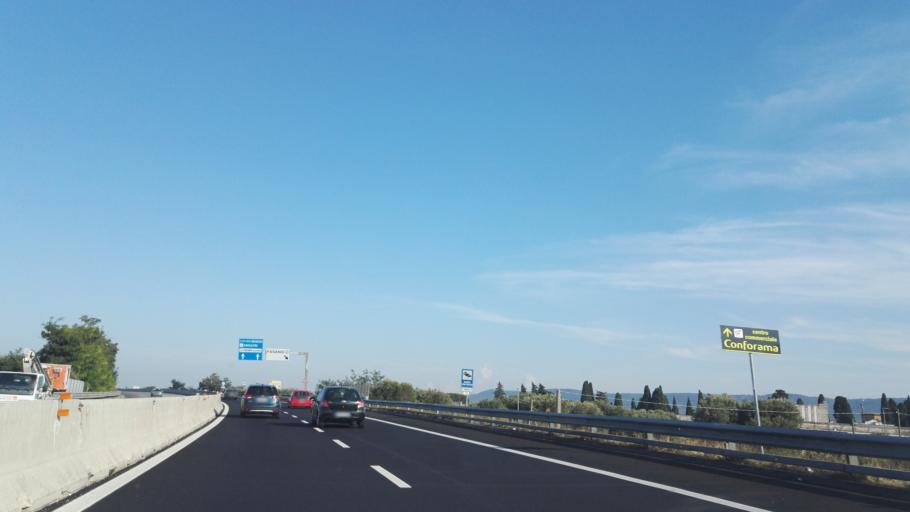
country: IT
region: Apulia
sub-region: Provincia di Brindisi
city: Fasano
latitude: 40.8428
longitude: 17.3663
